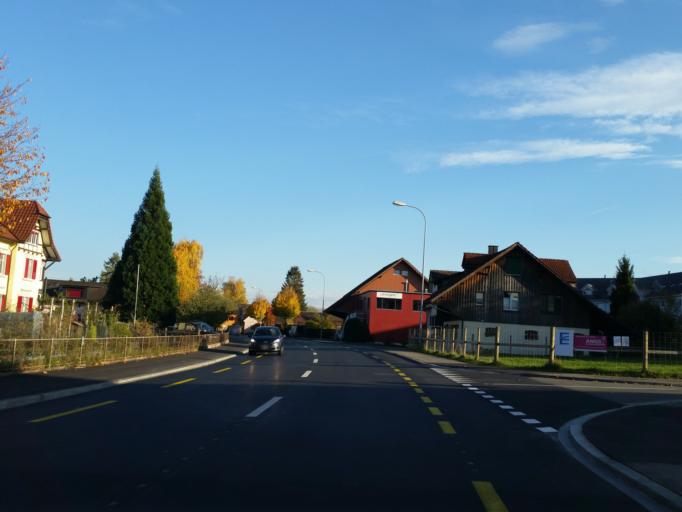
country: CH
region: Thurgau
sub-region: Arbon District
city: Uttwil
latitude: 47.5818
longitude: 9.3443
